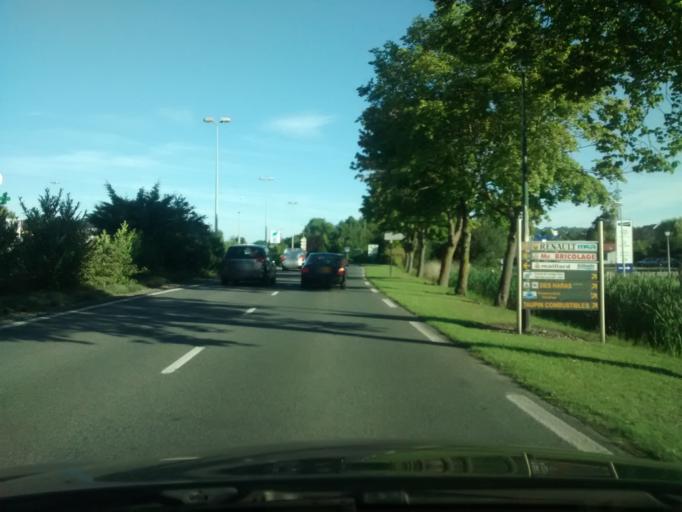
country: FR
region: Lower Normandy
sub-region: Departement du Calvados
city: Touques
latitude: 49.3460
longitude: 0.0983
